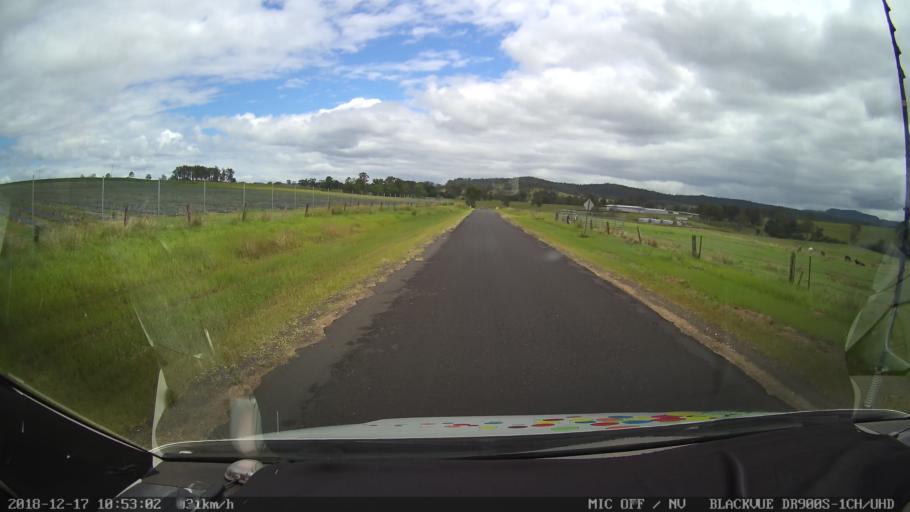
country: AU
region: New South Wales
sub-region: Tenterfield Municipality
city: Carrolls Creek
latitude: -28.8411
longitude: 152.5626
